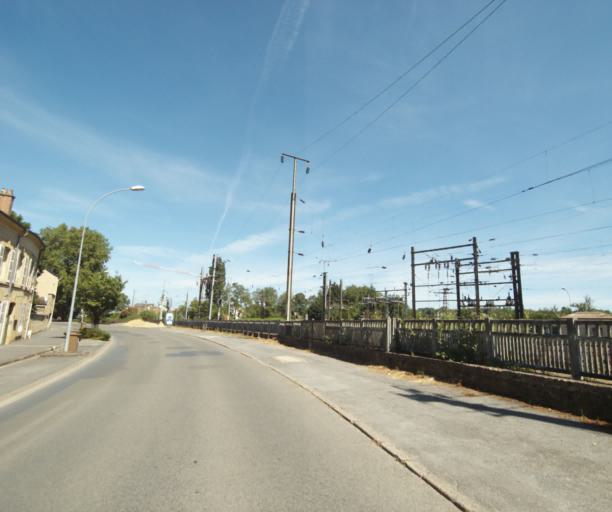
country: FR
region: Champagne-Ardenne
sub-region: Departement des Ardennes
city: Villers-Semeuse
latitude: 49.7512
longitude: 4.7353
